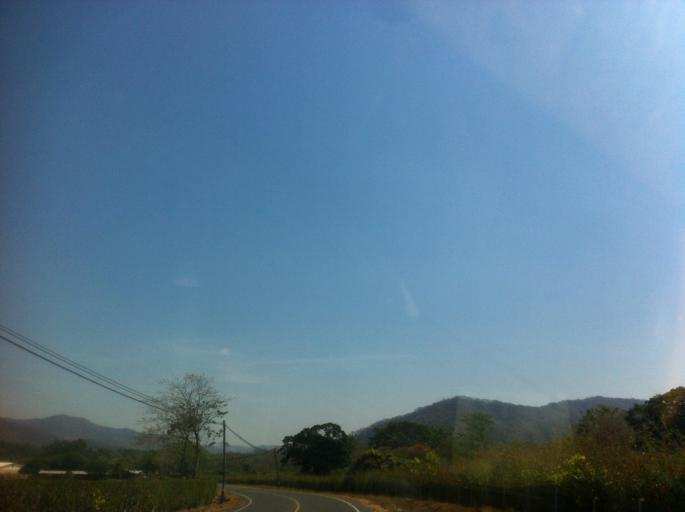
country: CR
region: Guanacaste
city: Hojancha
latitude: 10.0802
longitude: -85.4673
